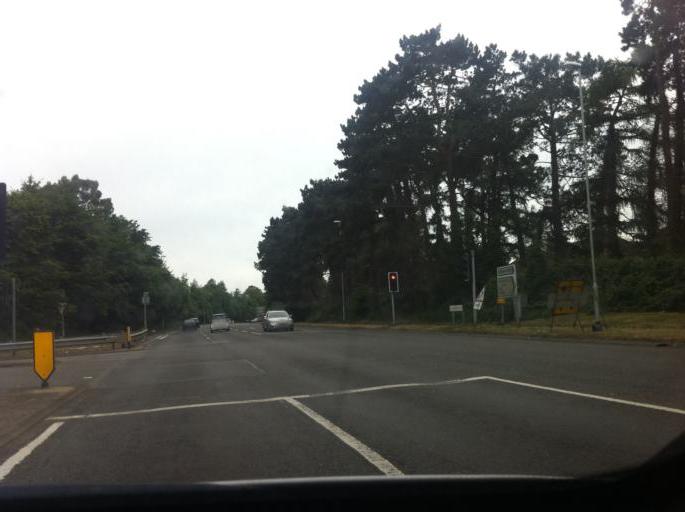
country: GB
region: England
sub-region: Northamptonshire
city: Northampton
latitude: 52.2541
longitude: -0.8365
